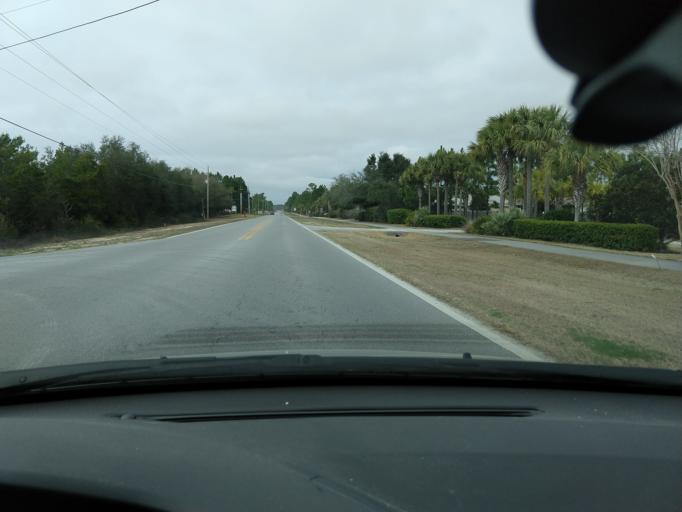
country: US
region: Florida
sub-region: Walton County
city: Miramar Beach
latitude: 30.3635
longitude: -86.2654
